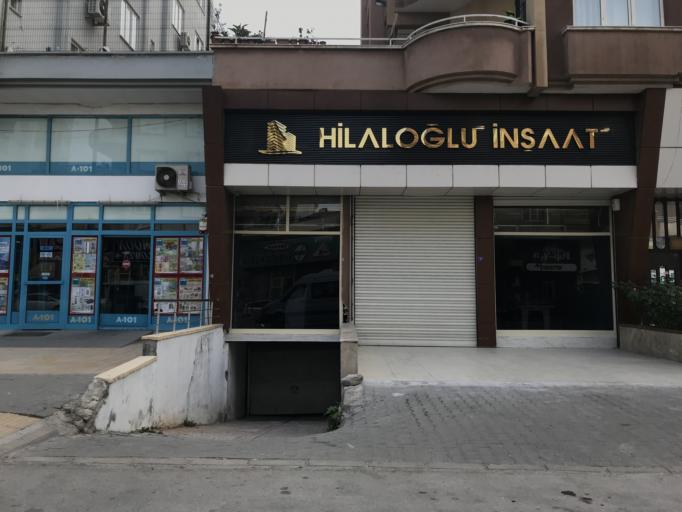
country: TR
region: Gaziantep
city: Sahinbey
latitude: 37.0531
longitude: 37.3347
